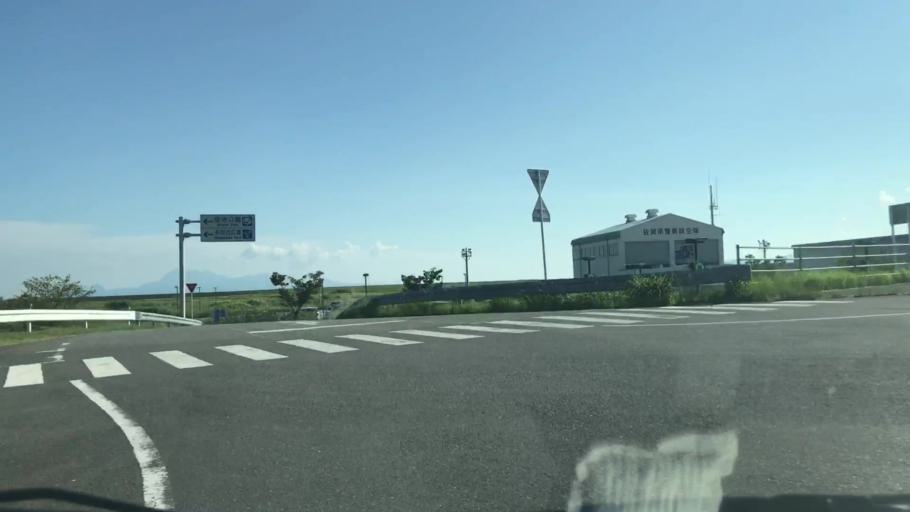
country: JP
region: Saga Prefecture
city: Okawa
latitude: 33.1533
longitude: 130.3075
